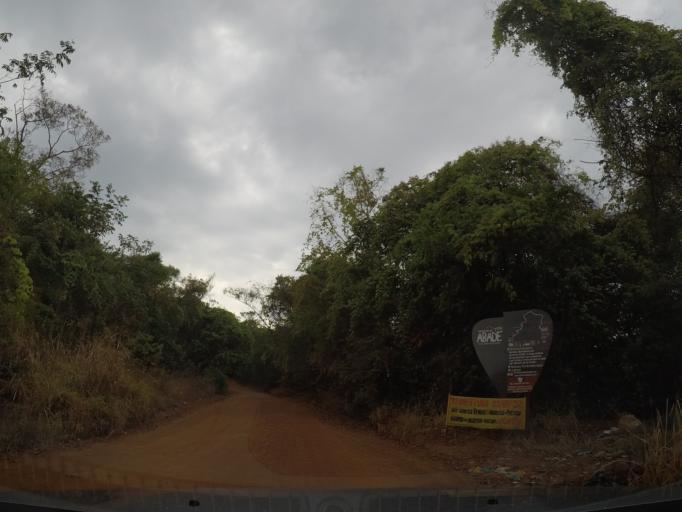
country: BR
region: Goias
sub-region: Pirenopolis
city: Pirenopolis
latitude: -15.8437
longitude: -48.9166
